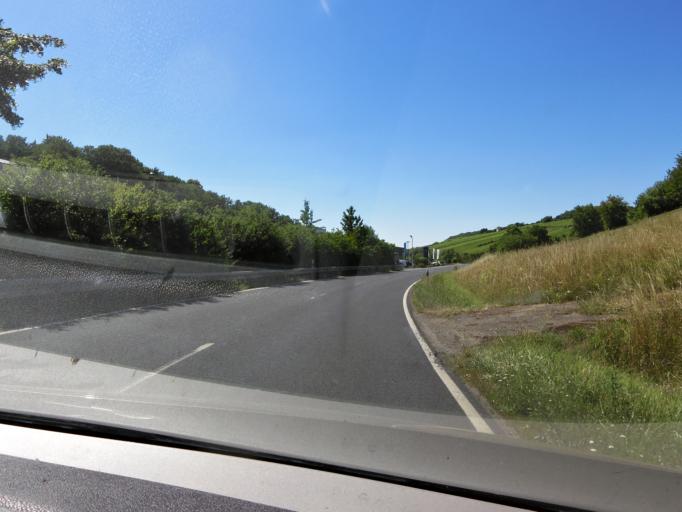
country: DE
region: Bavaria
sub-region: Regierungsbezirk Unterfranken
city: Theilheim
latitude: 49.7527
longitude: 10.0179
